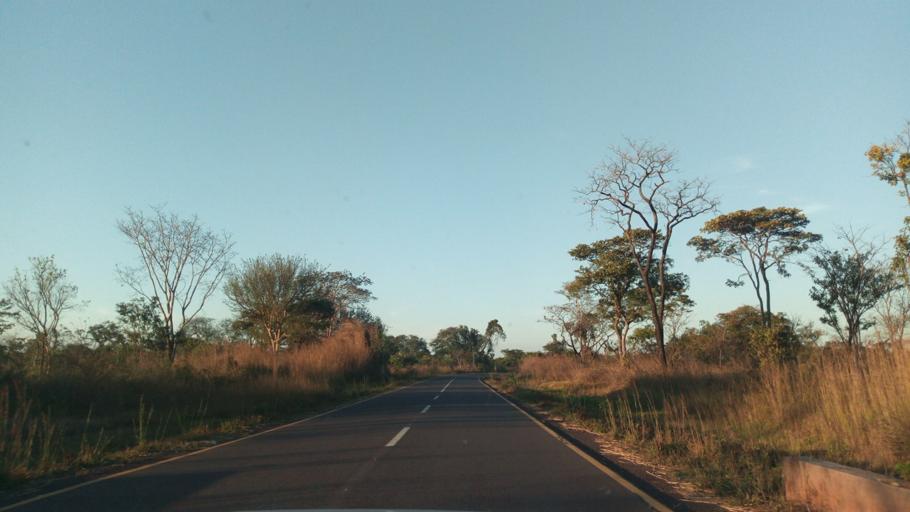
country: ZM
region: Luapula
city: Mwense
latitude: -10.7760
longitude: 28.2505
